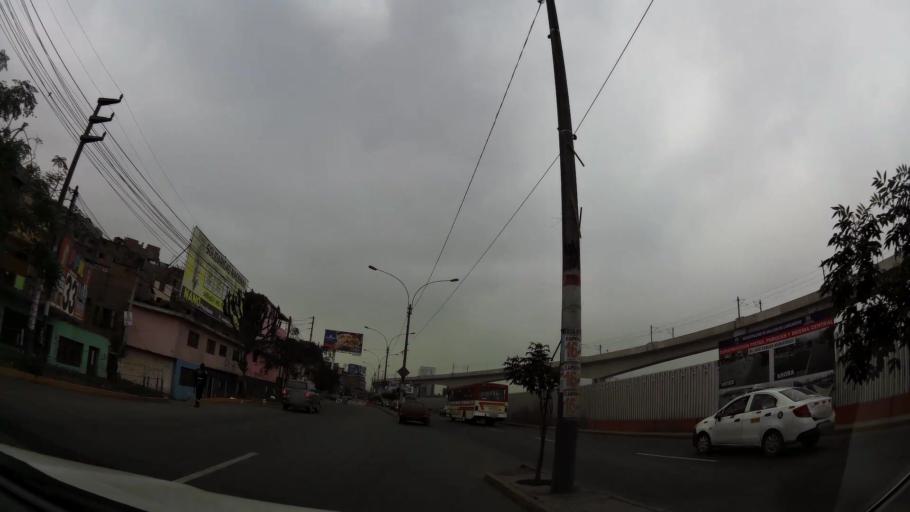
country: PE
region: Lima
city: Lima
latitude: -12.0349
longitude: -77.0127
